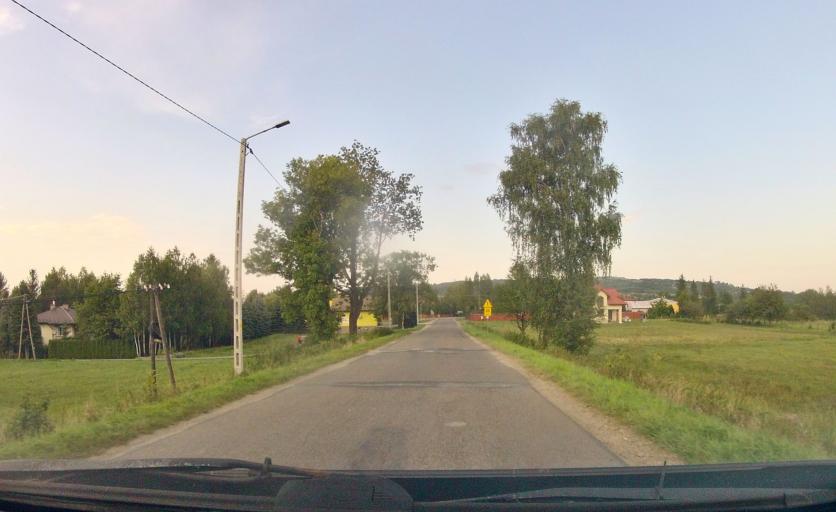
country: PL
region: Subcarpathian Voivodeship
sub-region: Powiat krosnienski
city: Dukla
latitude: 49.5570
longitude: 21.6260
